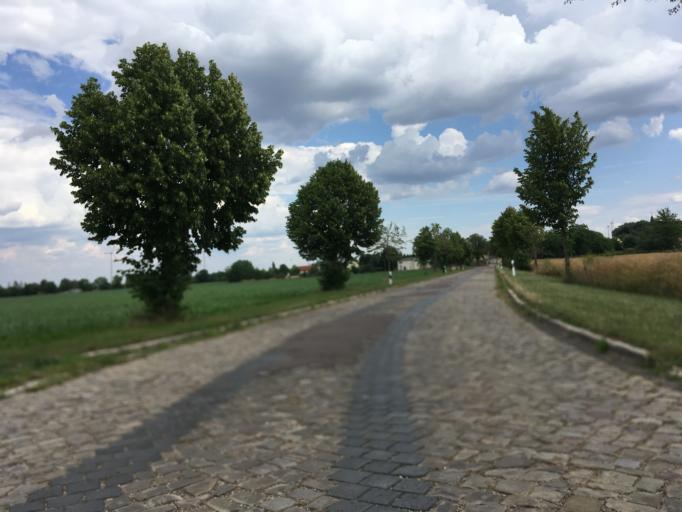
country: DE
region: Saxony-Anhalt
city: Baalberge
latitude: 51.7773
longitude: 11.8184
